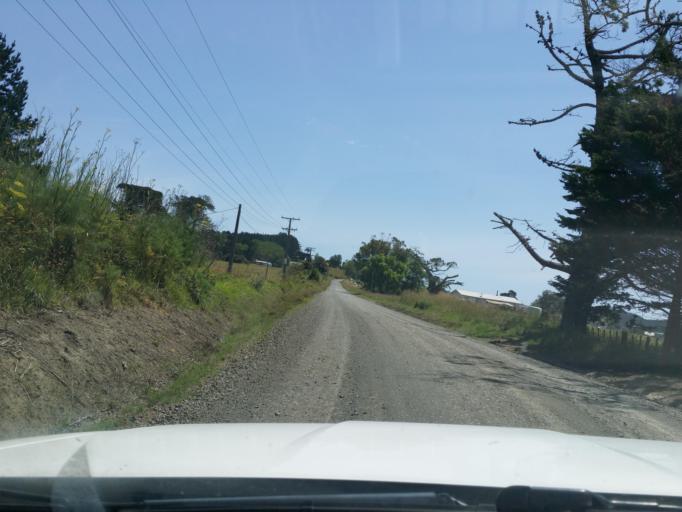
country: NZ
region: Northland
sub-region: Kaipara District
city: Dargaville
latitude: -35.9065
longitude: 173.8030
